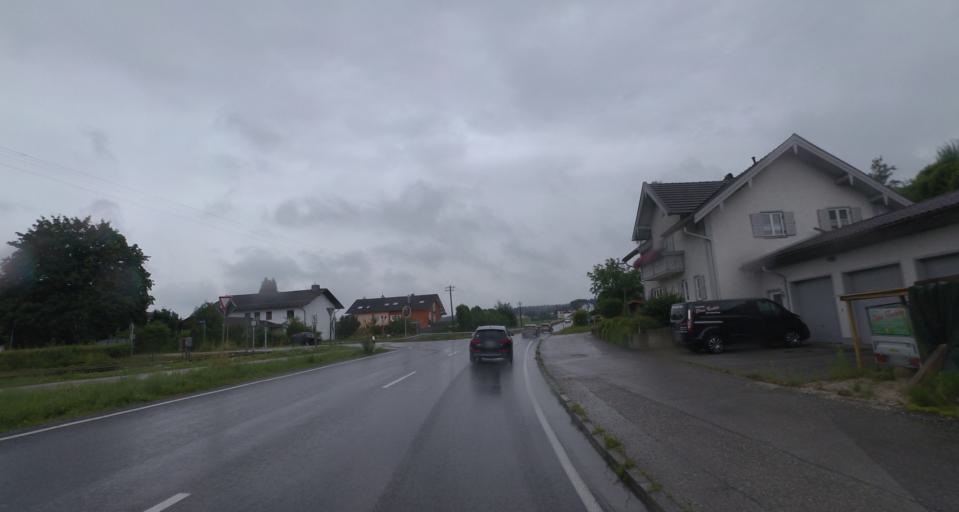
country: DE
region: Bavaria
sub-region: Upper Bavaria
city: Traunreut
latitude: 47.9616
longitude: 12.5689
